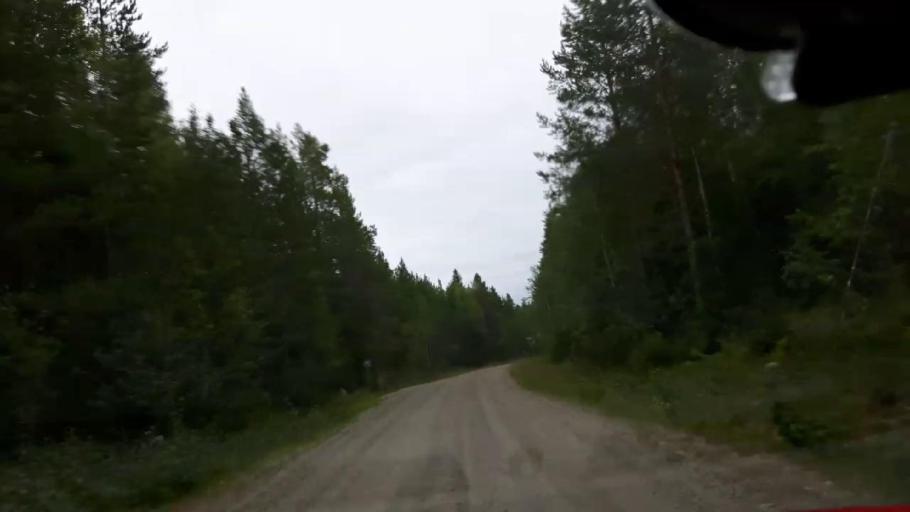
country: SE
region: Vaesternorrland
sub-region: Ange Kommun
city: Ange
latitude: 62.8100
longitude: 15.7352
